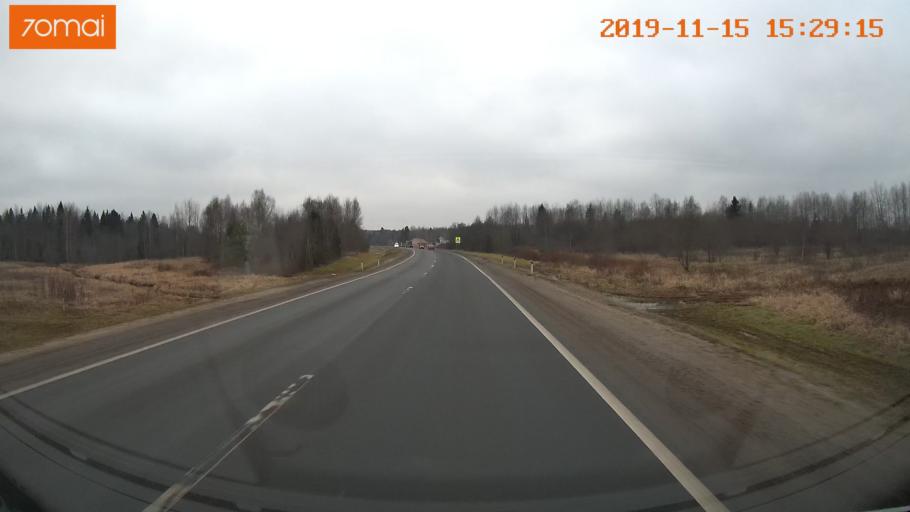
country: RU
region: Jaroslavl
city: Danilov
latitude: 58.1228
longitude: 40.1224
